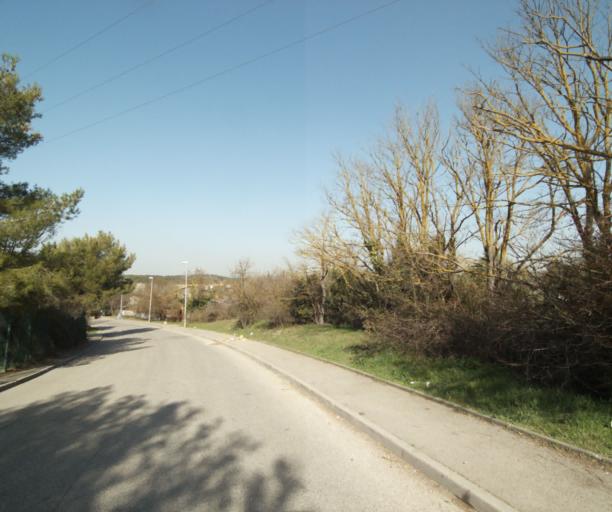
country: FR
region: Provence-Alpes-Cote d'Azur
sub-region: Departement des Bouches-du-Rhone
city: Cabries
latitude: 43.4223
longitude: 5.3925
